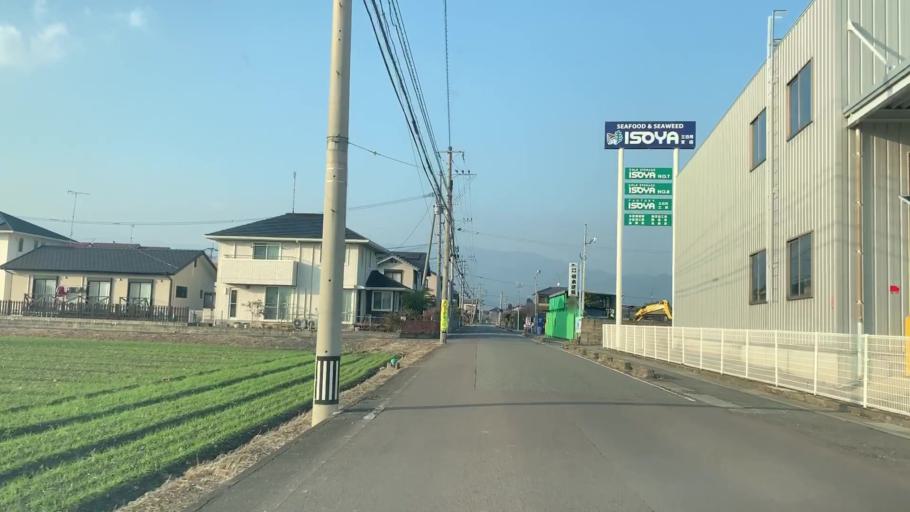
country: JP
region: Saga Prefecture
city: Saga-shi
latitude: 33.2681
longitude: 130.2301
